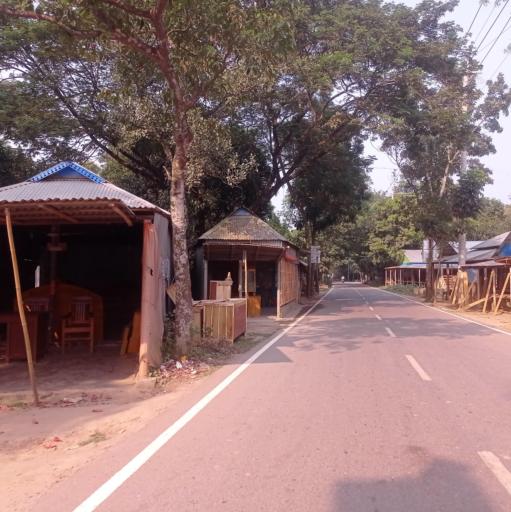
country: BD
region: Dhaka
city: Bhairab Bazar
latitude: 24.0838
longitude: 90.8495
